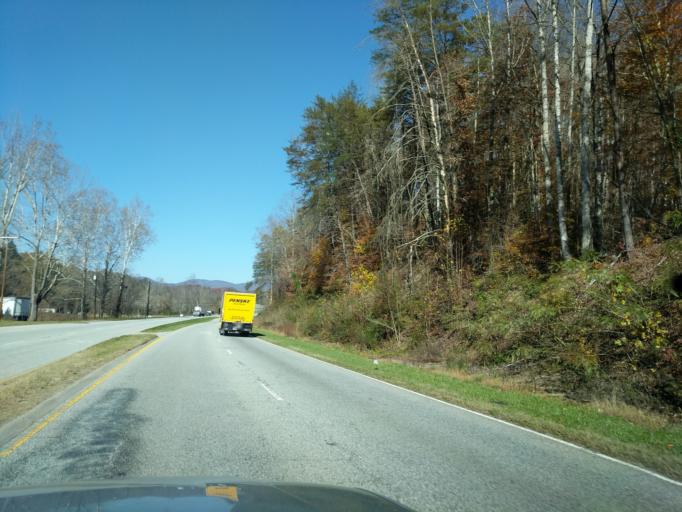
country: US
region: South Carolina
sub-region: Greenville County
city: Slater-Marietta
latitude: 35.0793
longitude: -82.4458
